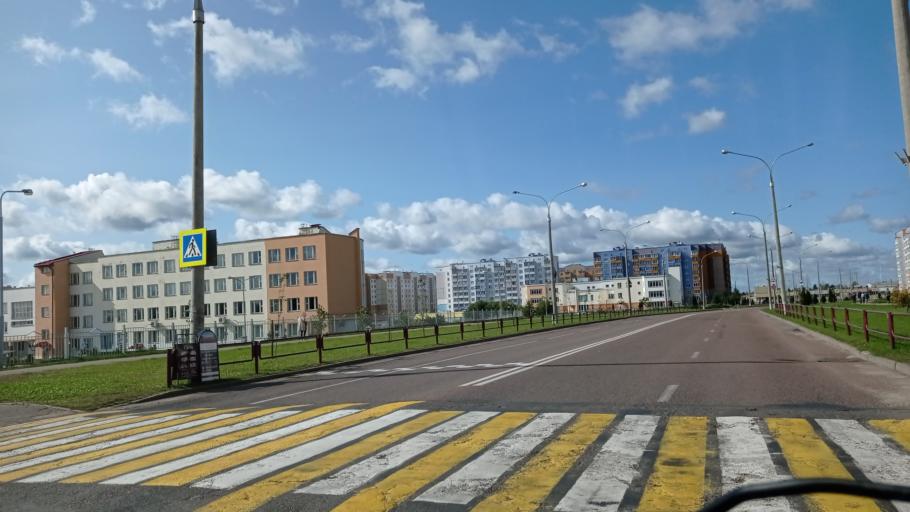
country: BY
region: Vitebsk
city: Vitebsk
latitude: 55.1691
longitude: 30.2636
